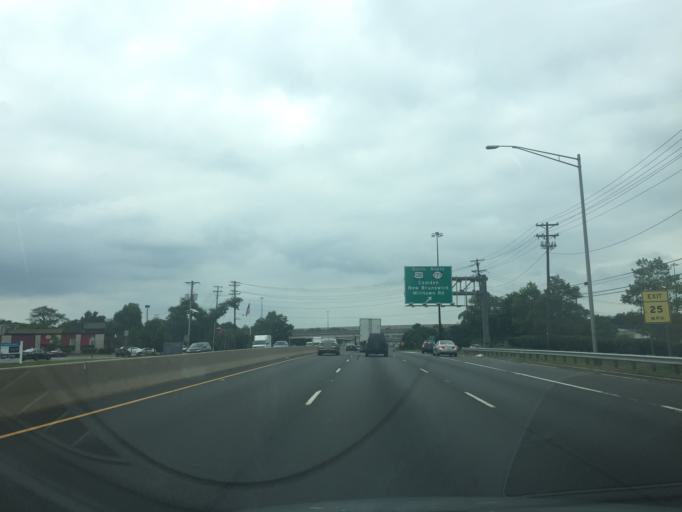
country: US
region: New Jersey
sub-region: Middlesex County
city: Milltown
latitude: 40.4616
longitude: -74.4591
